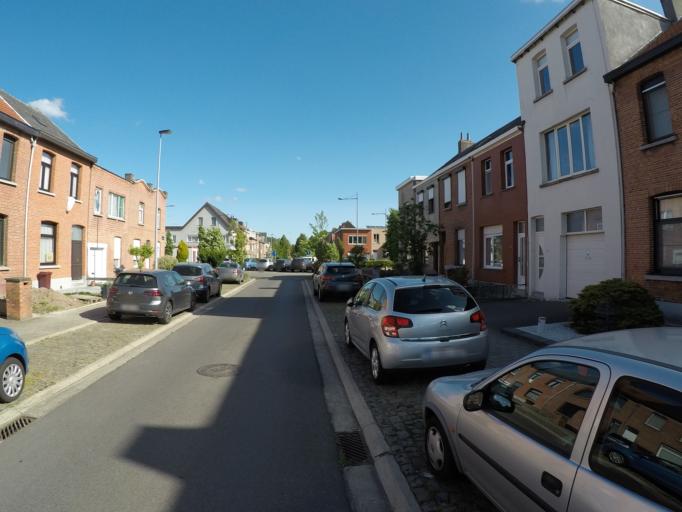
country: BE
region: Flanders
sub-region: Provincie Antwerpen
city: Schoten
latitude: 51.2500
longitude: 4.4828
